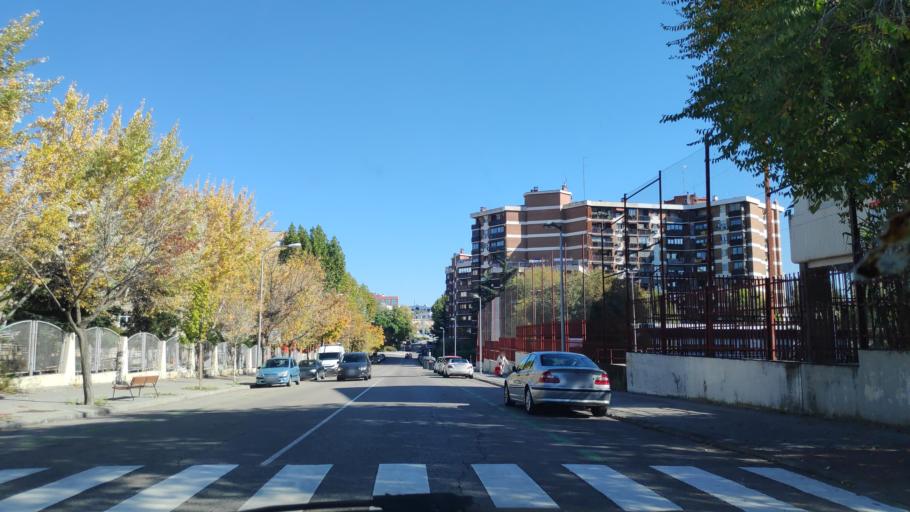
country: ES
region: Madrid
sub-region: Provincia de Madrid
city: Tetuan de las Victorias
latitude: 40.4875
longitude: -3.7009
